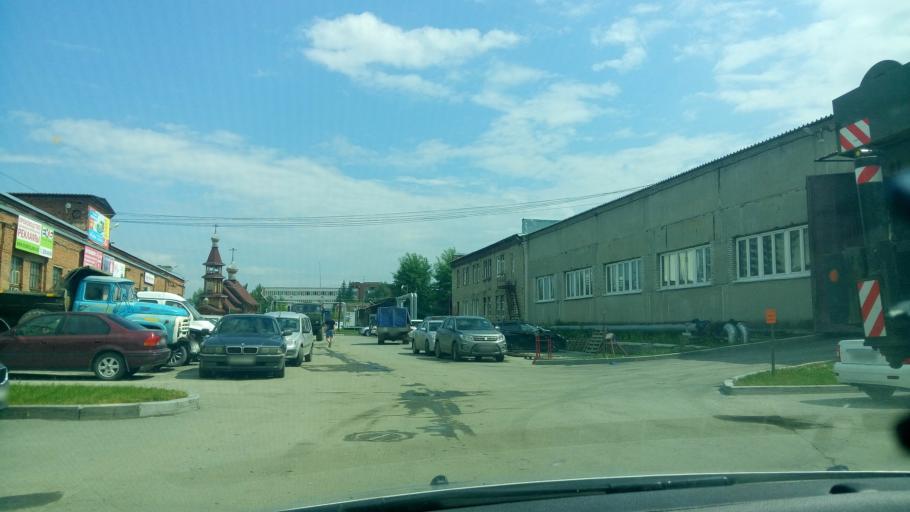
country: RU
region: Sverdlovsk
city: Yekaterinburg
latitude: 56.8567
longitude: 60.6603
